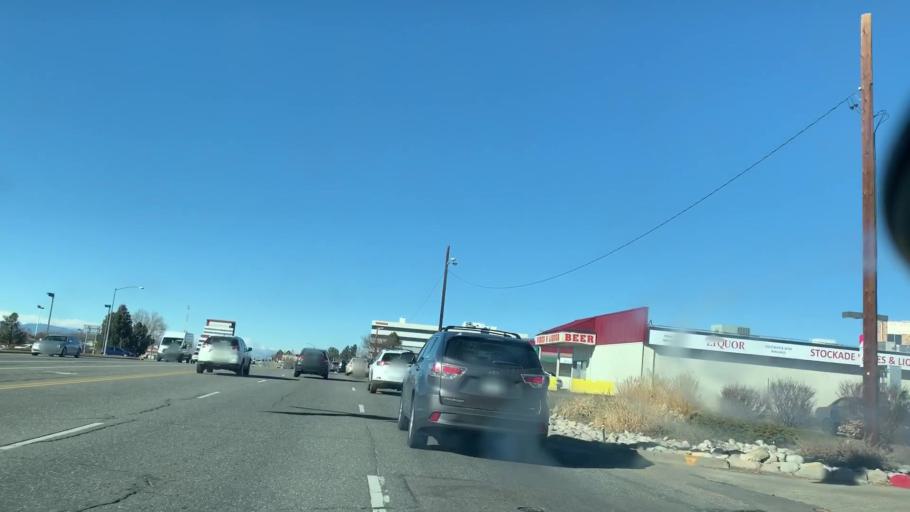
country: US
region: Colorado
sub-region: Adams County
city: Aurora
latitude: 39.6677
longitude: -104.8621
